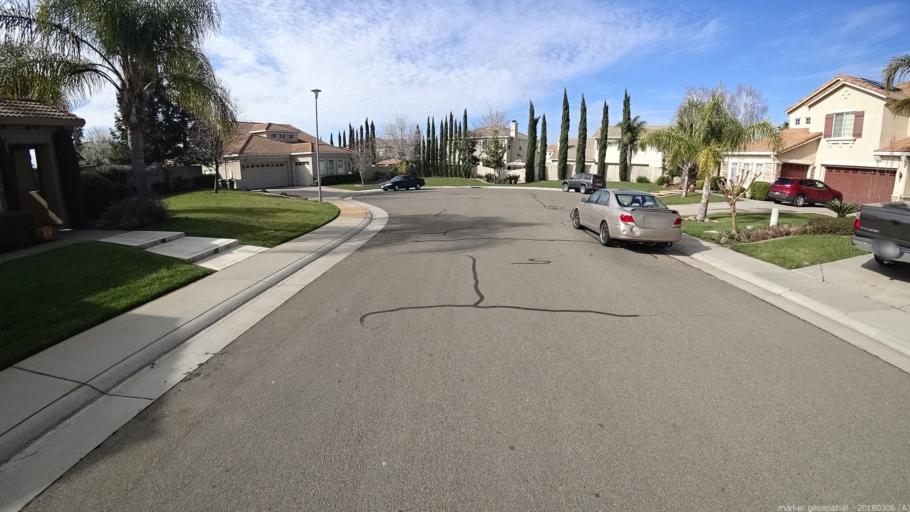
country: US
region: California
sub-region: Sacramento County
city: Vineyard
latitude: 38.4701
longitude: -121.3092
